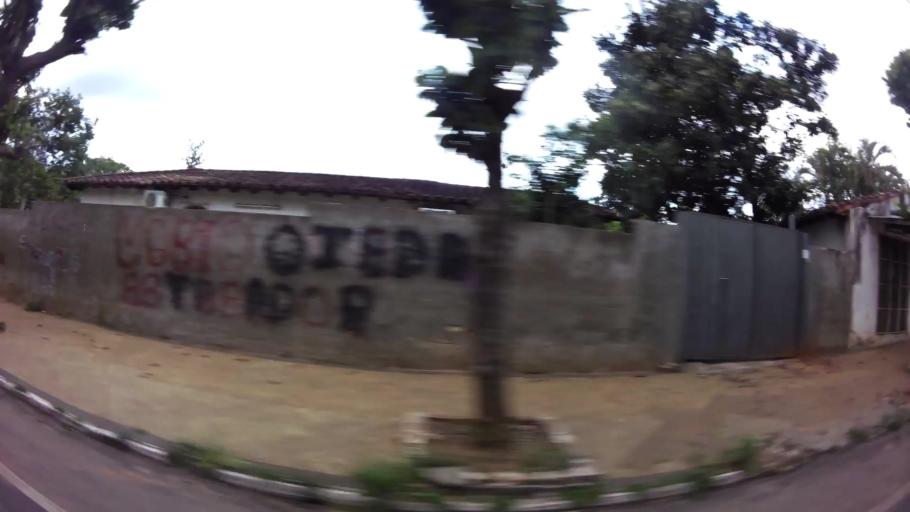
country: PY
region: Central
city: Fernando de la Mora
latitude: -25.3343
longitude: -57.5575
